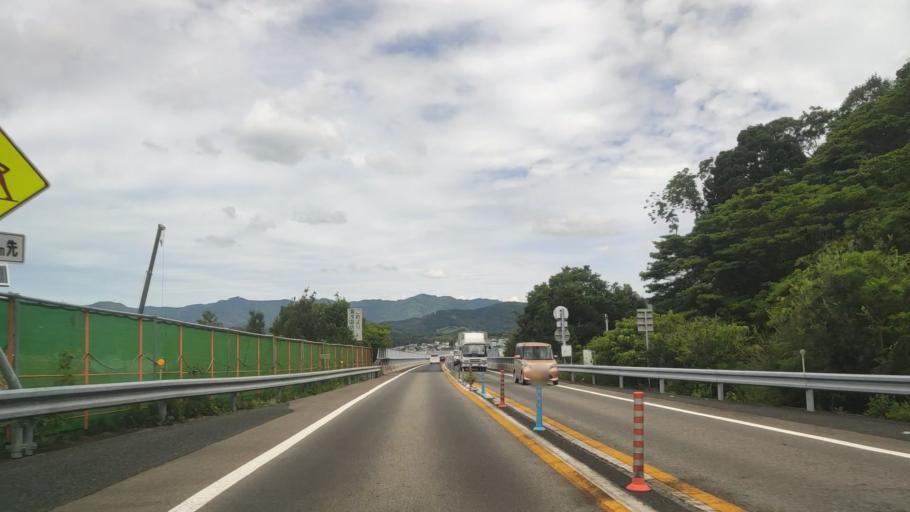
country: JP
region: Wakayama
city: Gobo
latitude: 33.8967
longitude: 135.1841
